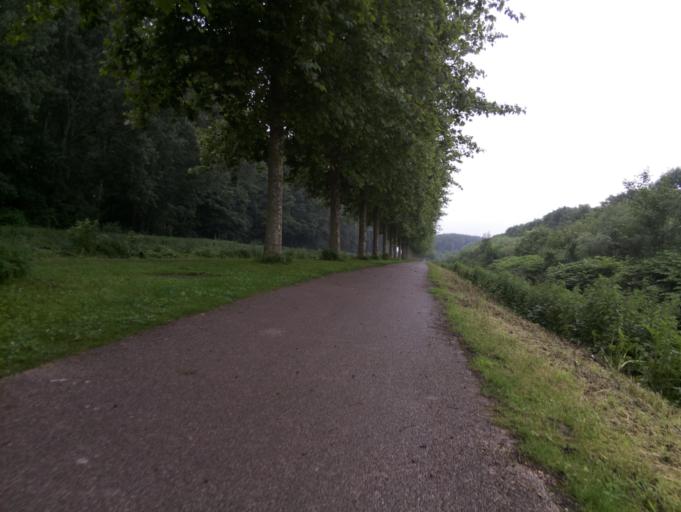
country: FR
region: Picardie
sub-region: Departement de la Somme
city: Dreuil-les-Amiens
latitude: 49.9190
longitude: 2.2562
